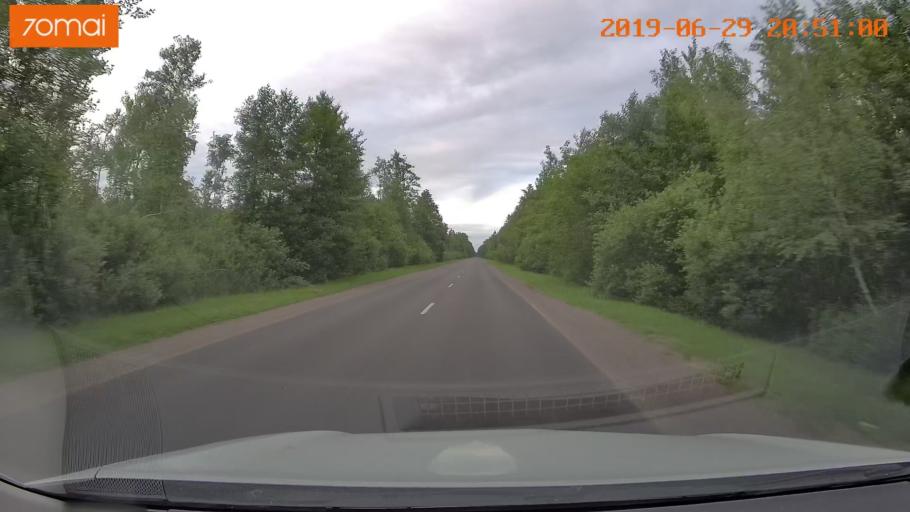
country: BY
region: Brest
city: Hantsavichy
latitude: 52.6830
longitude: 26.3435
